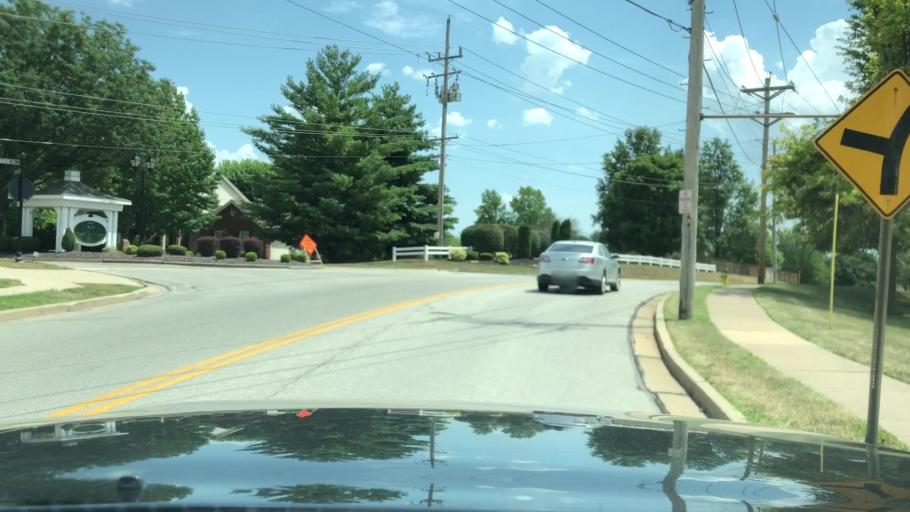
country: US
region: Missouri
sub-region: Saint Charles County
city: Saint Charles
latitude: 38.8018
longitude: -90.5310
